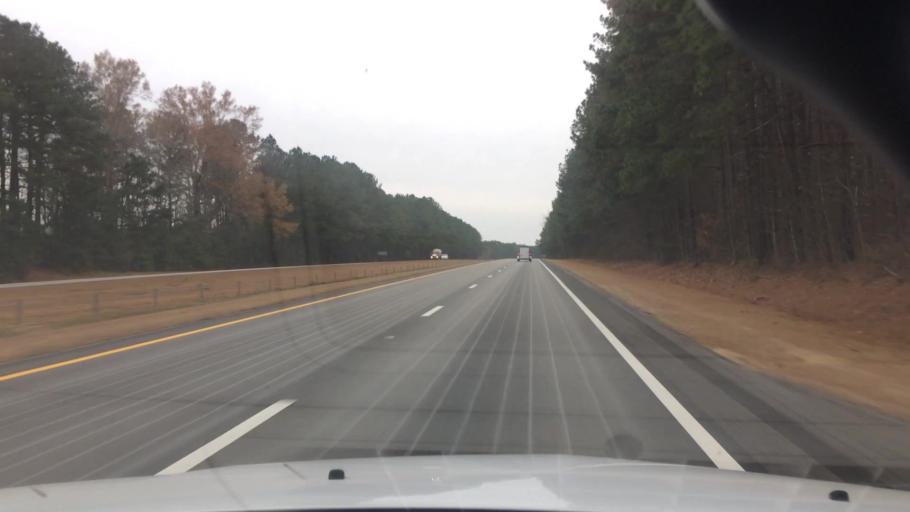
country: US
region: North Carolina
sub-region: Nash County
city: Spring Hope
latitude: 35.9006
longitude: -78.1849
